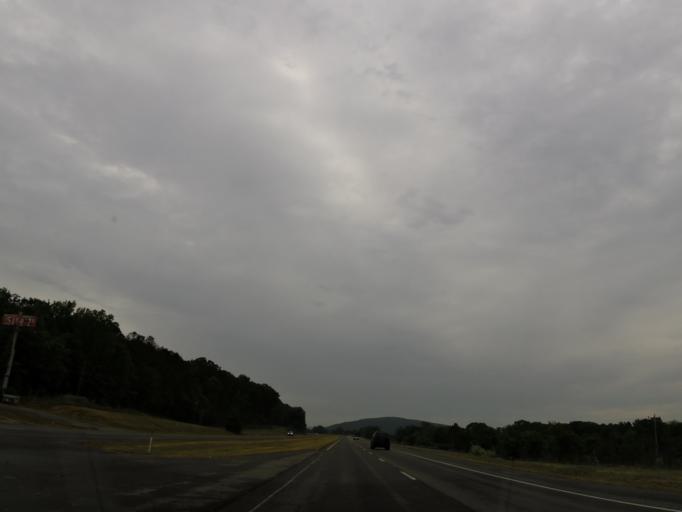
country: US
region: Alabama
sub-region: Madison County
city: Owens Cross Roads
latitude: 34.6916
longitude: -86.3542
